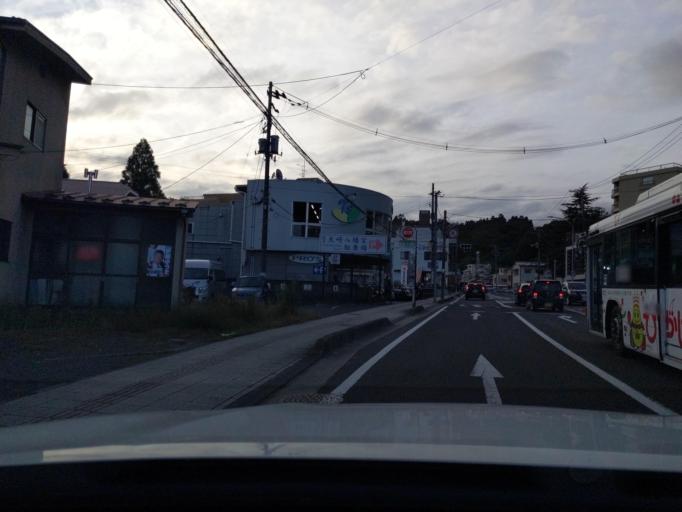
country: JP
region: Miyagi
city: Sendai
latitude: 38.2696
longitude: 140.8437
